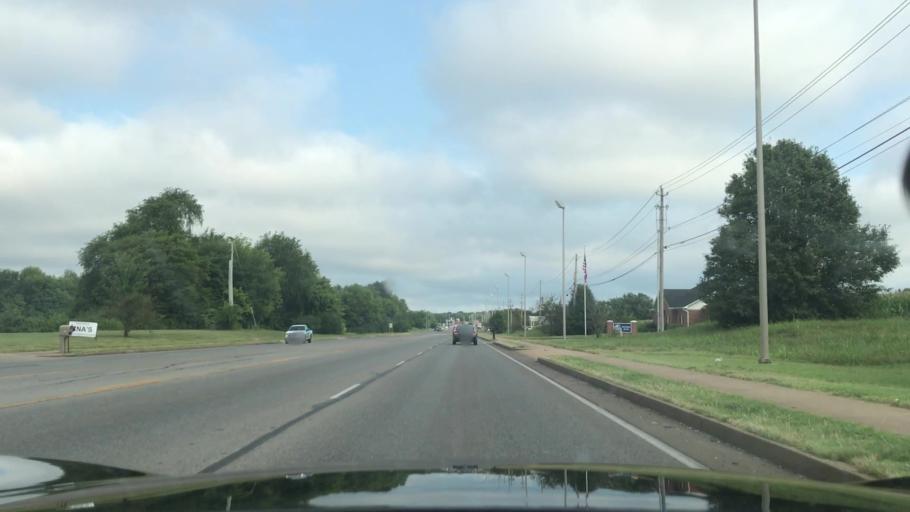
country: US
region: Kentucky
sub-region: Warren County
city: Bowling Green
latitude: 36.9541
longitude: -86.4441
